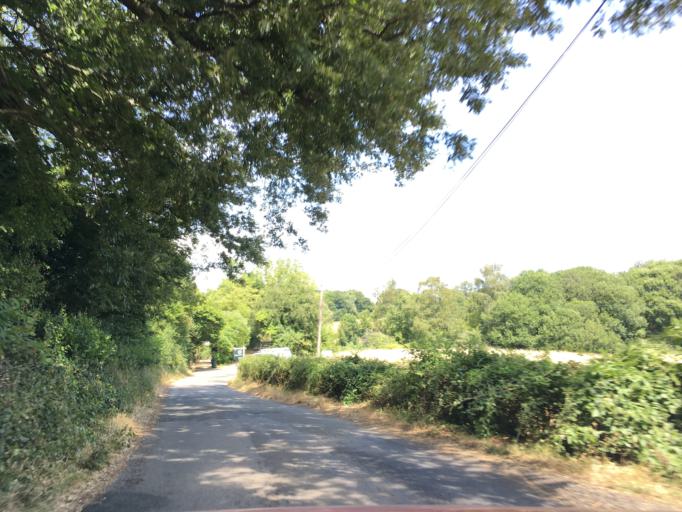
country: GB
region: Wales
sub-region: Caerphilly County Borough
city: Risca
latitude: 51.5872
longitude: -3.1131
